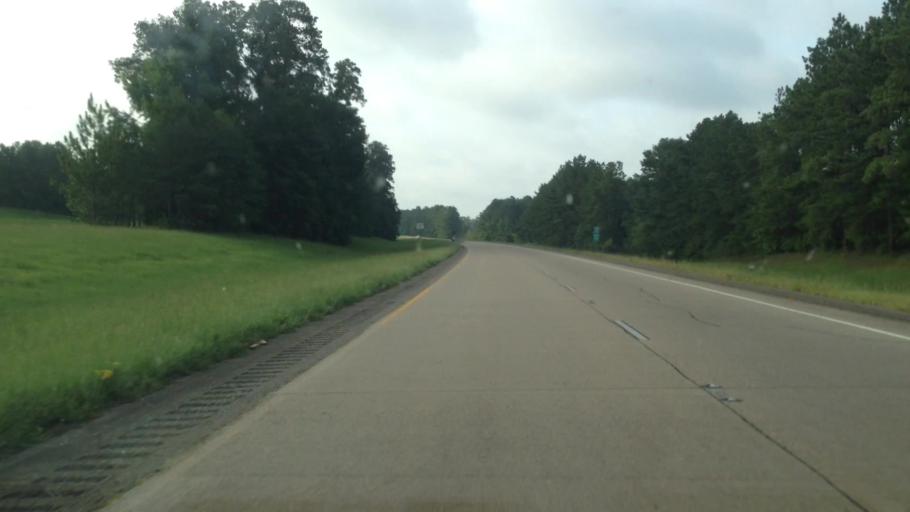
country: US
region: Louisiana
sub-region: Rapides Parish
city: Lecompte
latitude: 31.0366
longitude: -92.4139
